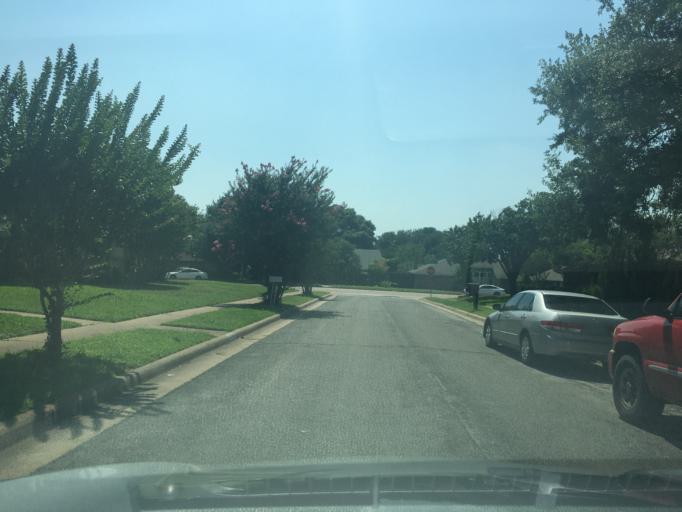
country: US
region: Texas
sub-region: Dallas County
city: Richardson
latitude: 32.9250
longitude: -96.7085
